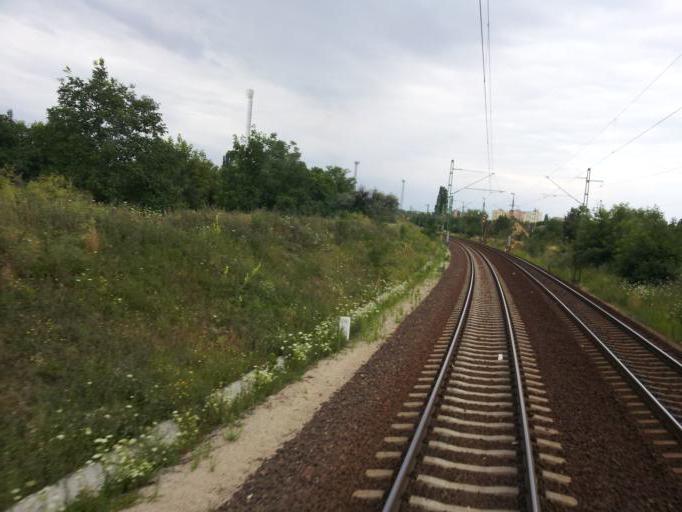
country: HU
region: Fejer
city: Szekesfehervar
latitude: 47.1859
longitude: 18.4384
